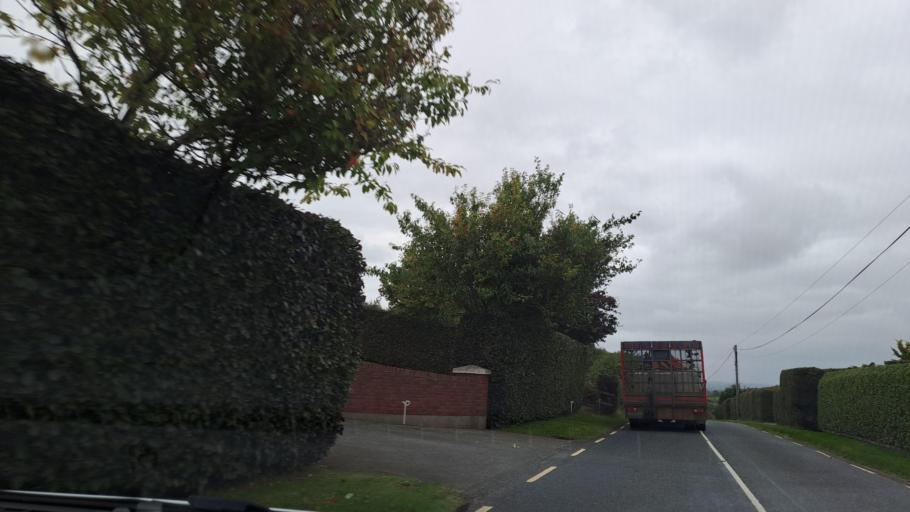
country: IE
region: Ulster
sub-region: County Monaghan
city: Castleblayney
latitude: 54.0886
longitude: -6.8312
